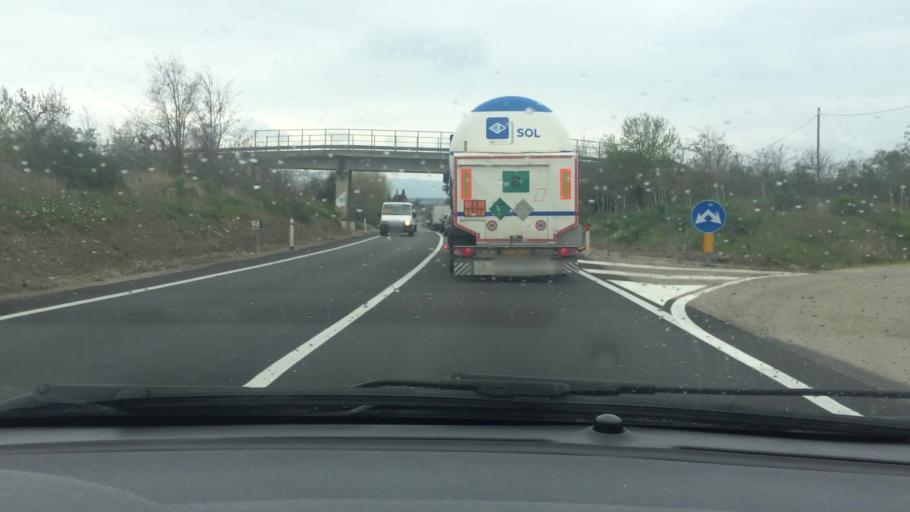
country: IT
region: Basilicate
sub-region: Provincia di Matera
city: Matera
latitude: 40.6153
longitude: 16.5778
